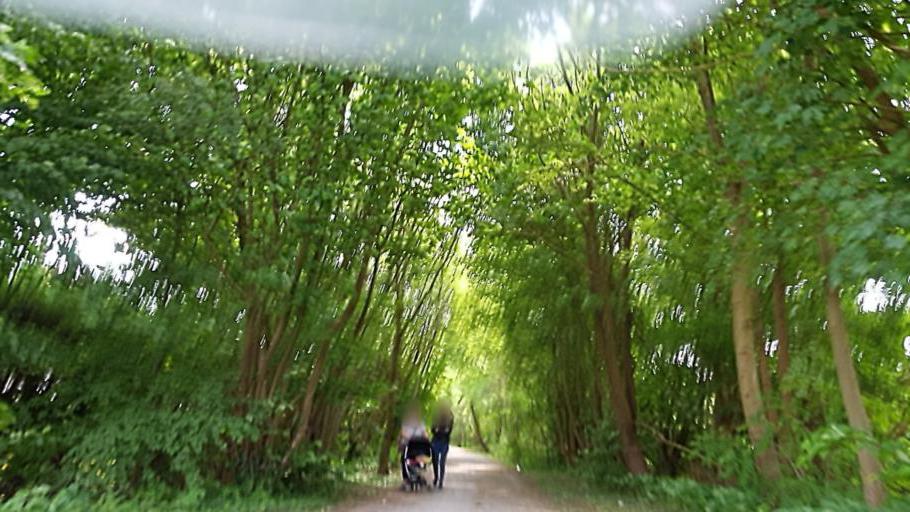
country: FR
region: Nord-Pas-de-Calais
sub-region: Departement du Nord
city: Vieux-Conde
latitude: 50.4676
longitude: 3.5734
